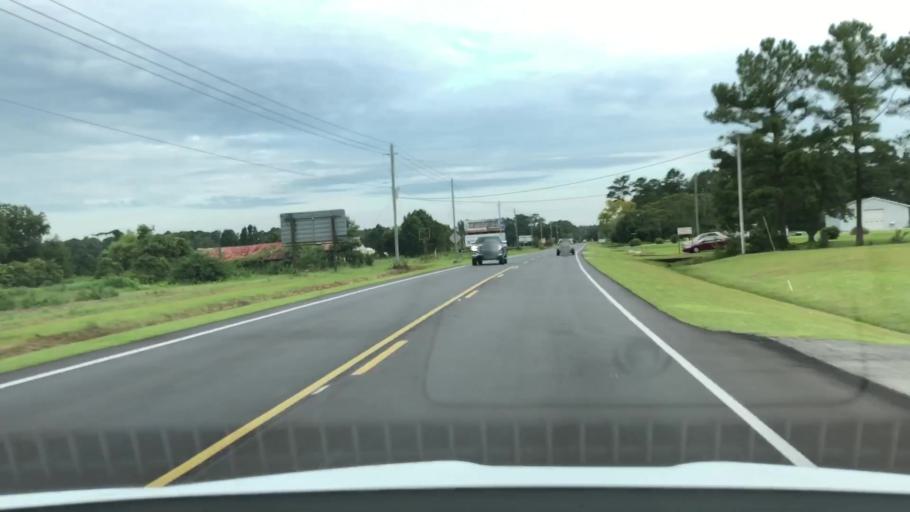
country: US
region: North Carolina
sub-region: Jones County
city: Maysville
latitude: 34.8619
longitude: -77.1894
